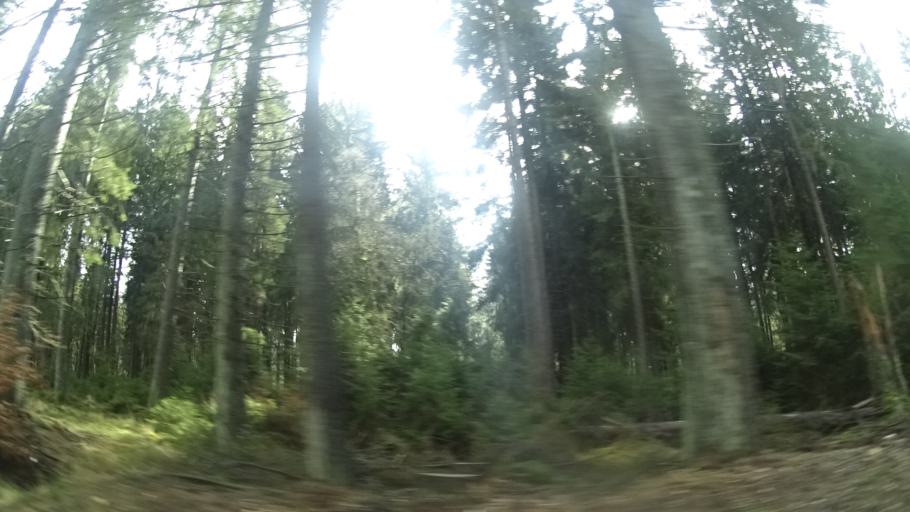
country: DE
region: Rheinland-Pfalz
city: Borfink
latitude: 49.7112
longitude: 7.1055
